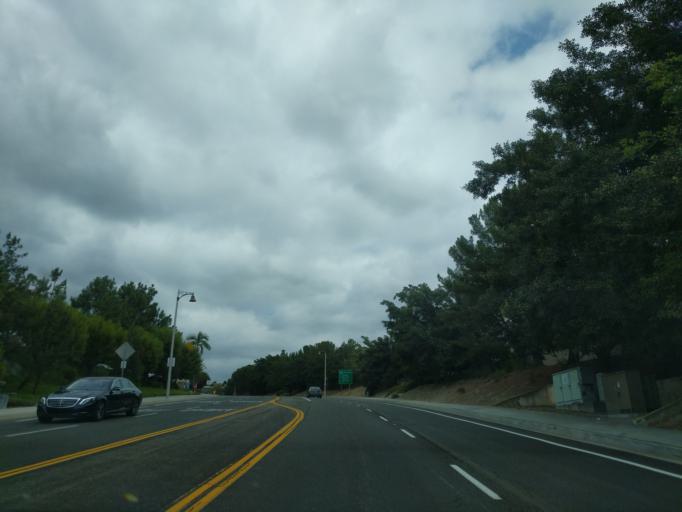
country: US
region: California
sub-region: Orange County
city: Portola Hills
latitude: 33.6536
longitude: -117.6283
